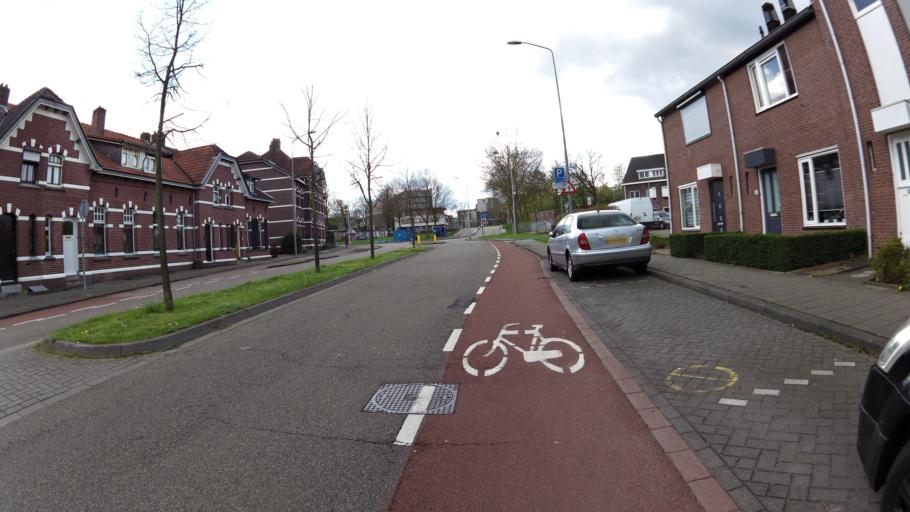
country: NL
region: Limburg
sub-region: Gemeente Heerlen
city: Heerlen
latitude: 50.8960
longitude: 5.9715
